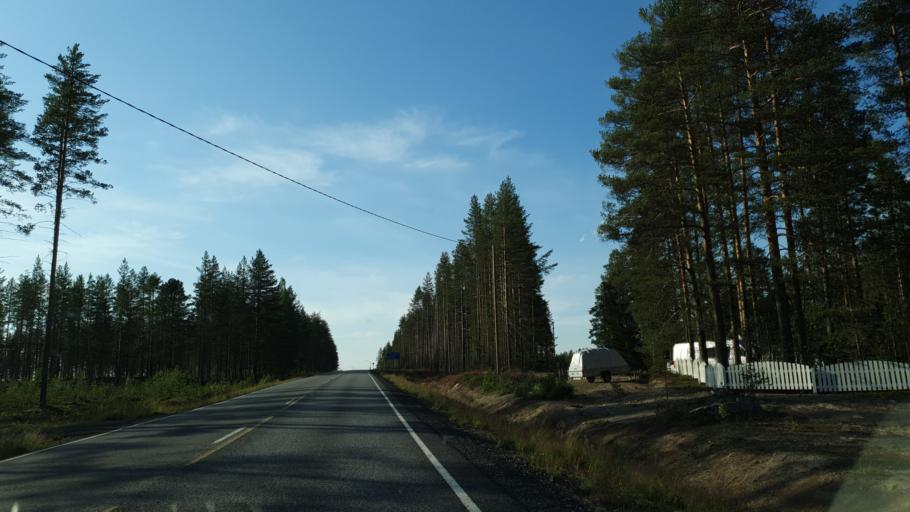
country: FI
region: Kainuu
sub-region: Kehys-Kainuu
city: Kuhmo
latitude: 64.0951
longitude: 29.4778
